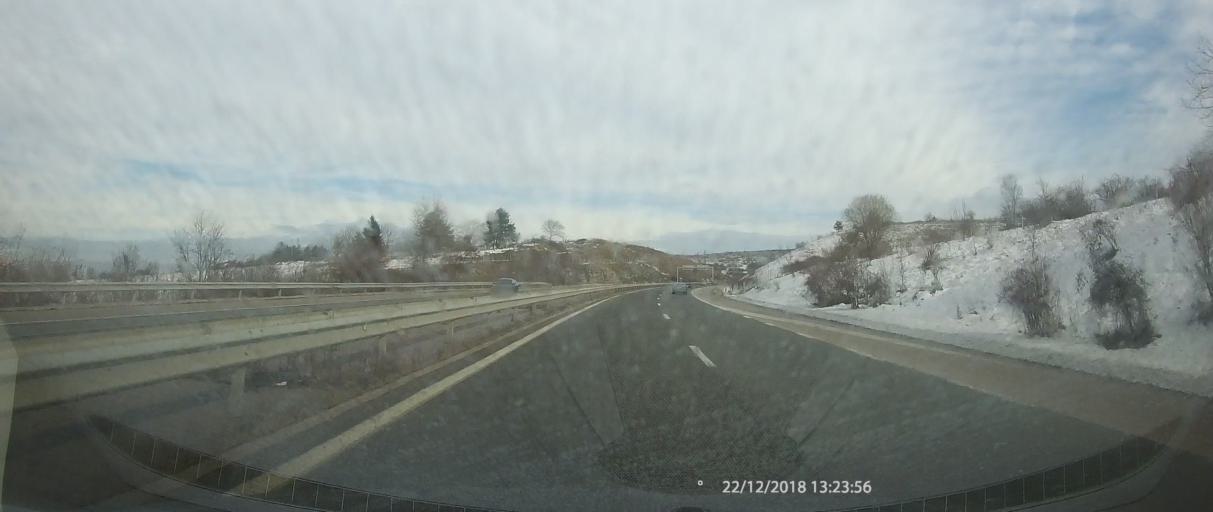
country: BG
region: Lovech
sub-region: Obshtina Yablanitsa
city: Yablanitsa
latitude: 43.0116
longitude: 24.0957
